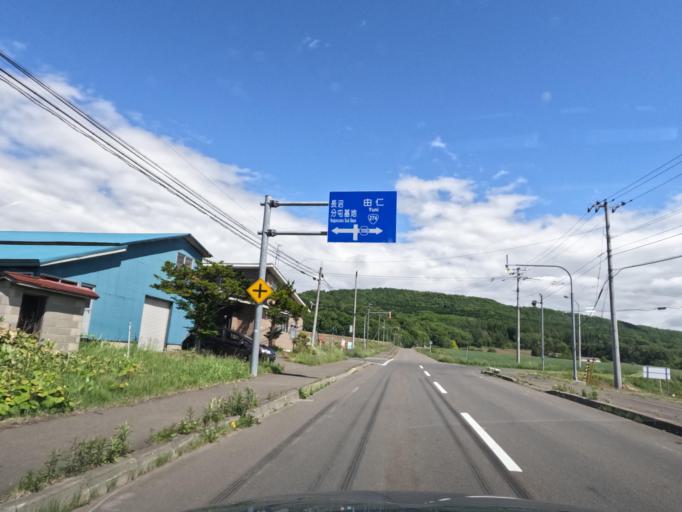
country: JP
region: Hokkaido
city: Kitahiroshima
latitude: 42.9969
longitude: 141.7290
